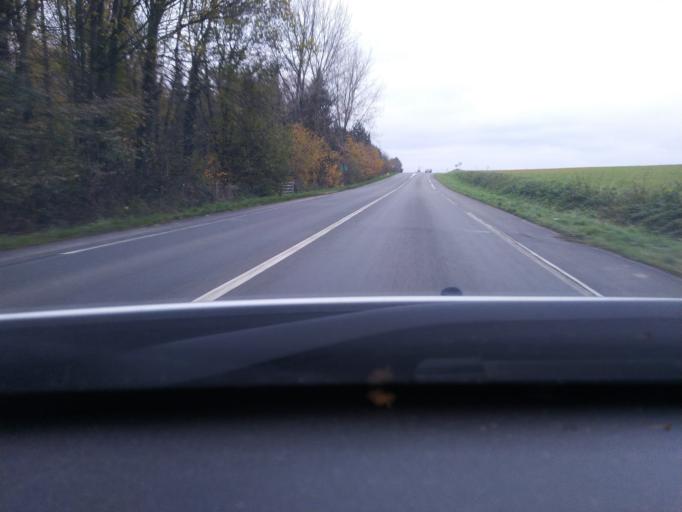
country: FR
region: Nord-Pas-de-Calais
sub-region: Departement du Pas-de-Calais
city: Hesdin
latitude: 50.3503
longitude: 2.0345
